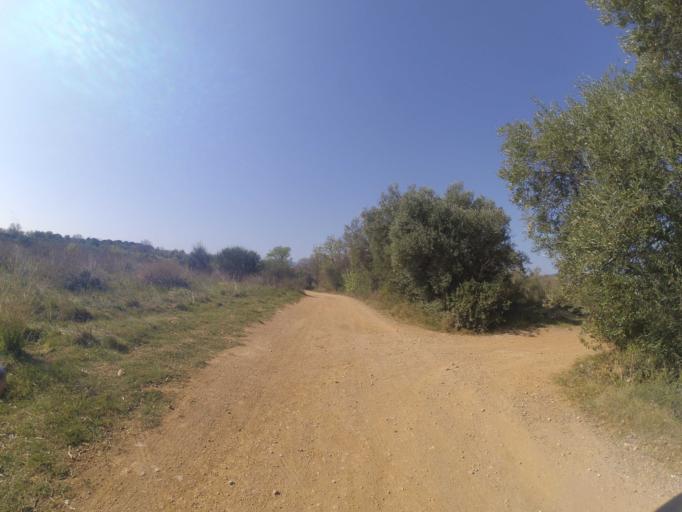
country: FR
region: Languedoc-Roussillon
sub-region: Departement des Pyrenees-Orientales
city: Llupia
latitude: 42.6138
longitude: 2.7638
